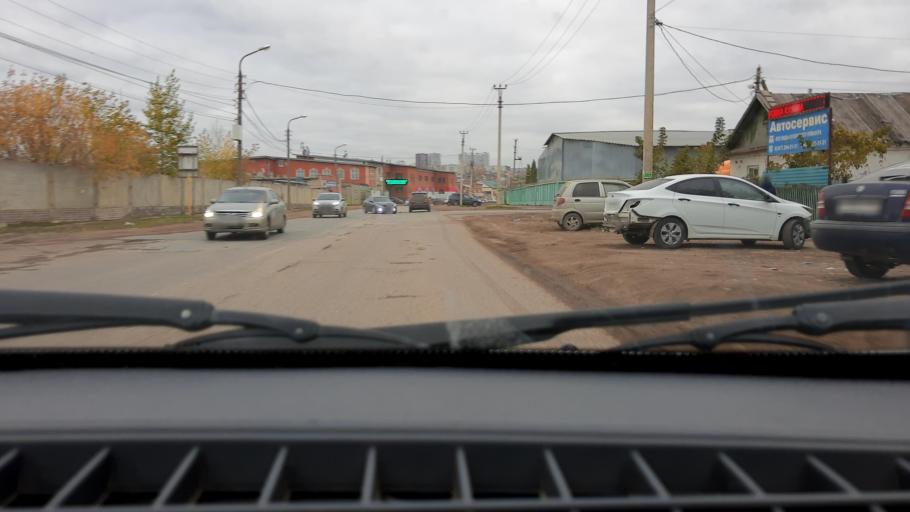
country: RU
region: Bashkortostan
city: Ufa
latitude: 54.7476
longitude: 55.9114
